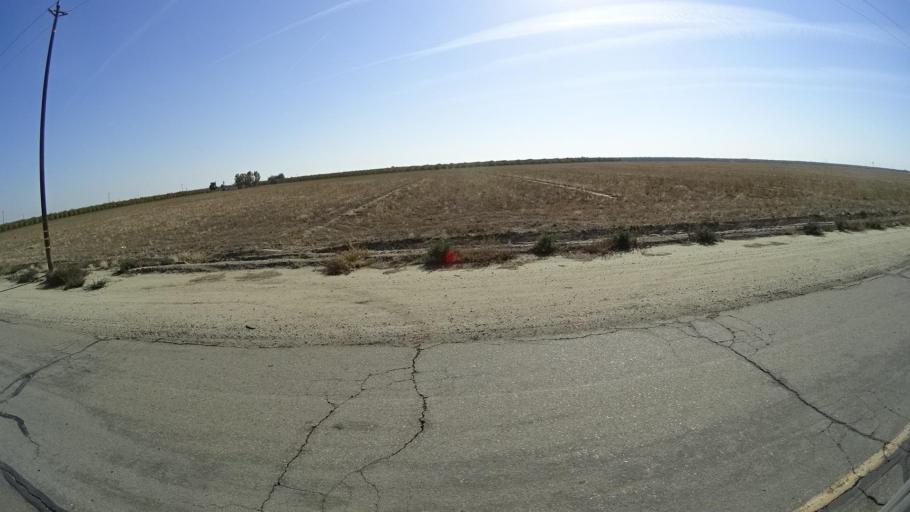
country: US
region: California
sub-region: Kern County
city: Wasco
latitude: 35.6670
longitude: -119.3775
